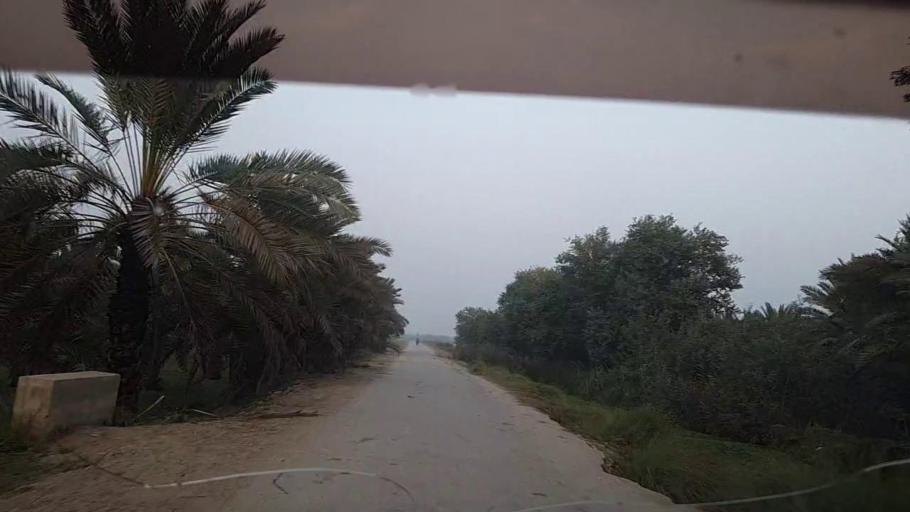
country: PK
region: Sindh
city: Khairpur
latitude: 27.5733
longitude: 68.7262
